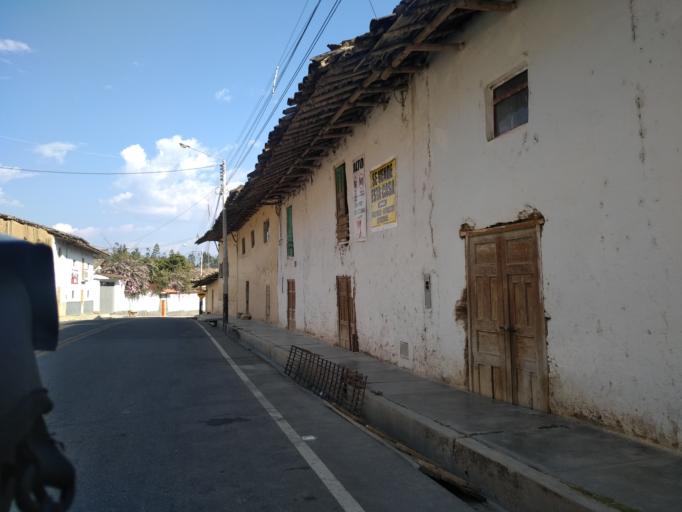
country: PE
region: Cajamarca
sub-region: San Marcos
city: San Marcos
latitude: -7.3858
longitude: -78.1248
